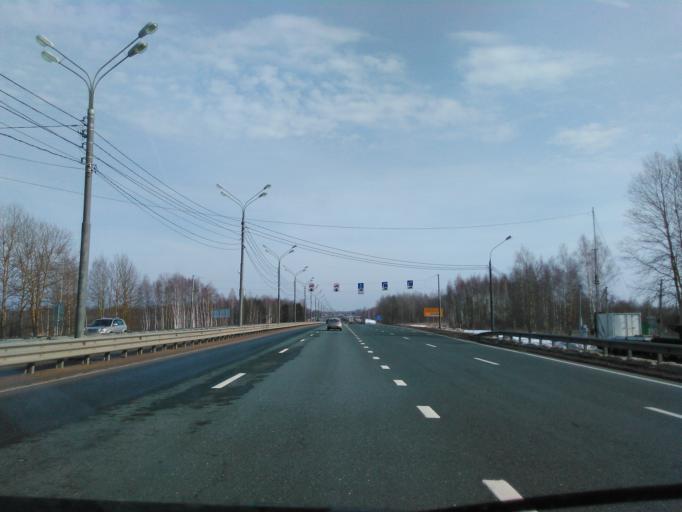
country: RU
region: Smolensk
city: Rudnya
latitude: 54.6908
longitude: 30.9906
